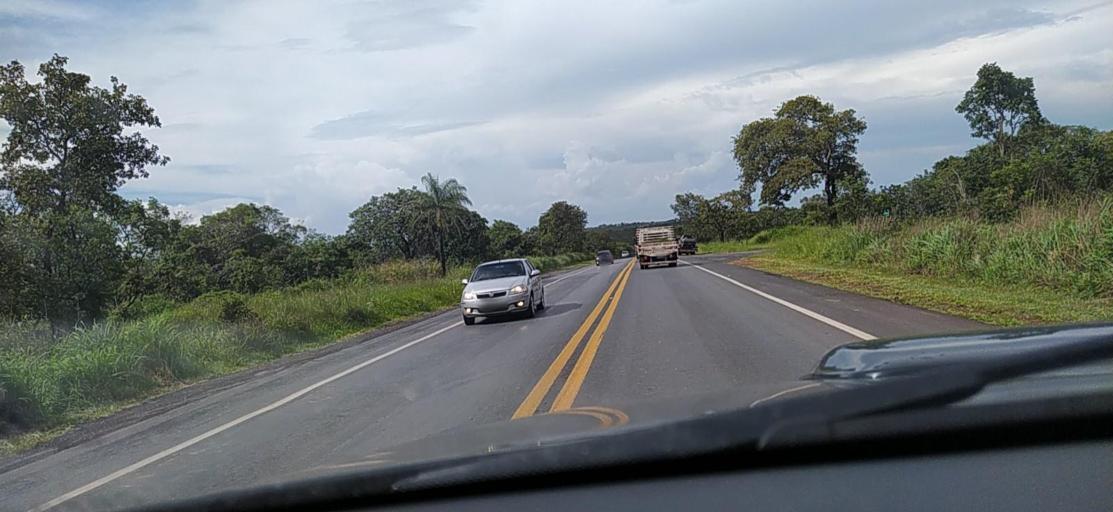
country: BR
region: Minas Gerais
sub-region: Montes Claros
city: Montes Claros
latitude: -16.8611
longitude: -43.8534
